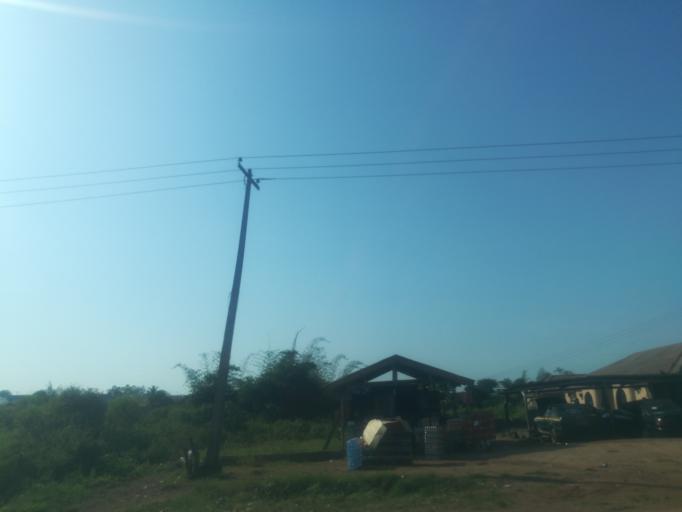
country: NG
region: Ogun
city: Abeokuta
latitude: 7.1728
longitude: 3.2738
